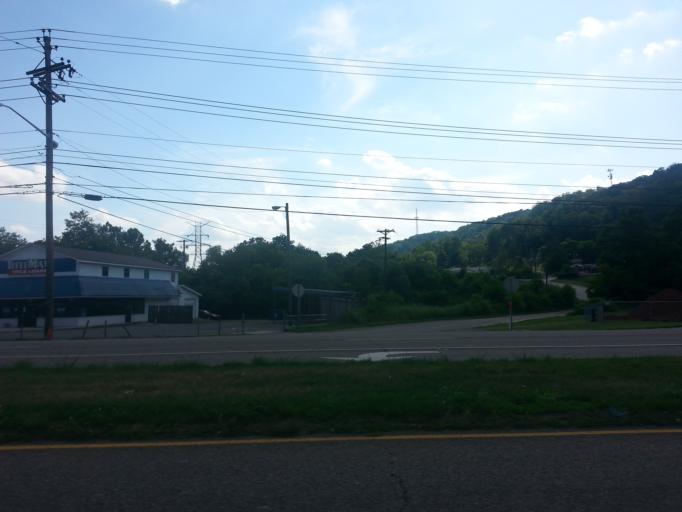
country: US
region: Tennessee
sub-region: Knox County
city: Knoxville
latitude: 36.0634
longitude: -83.9247
